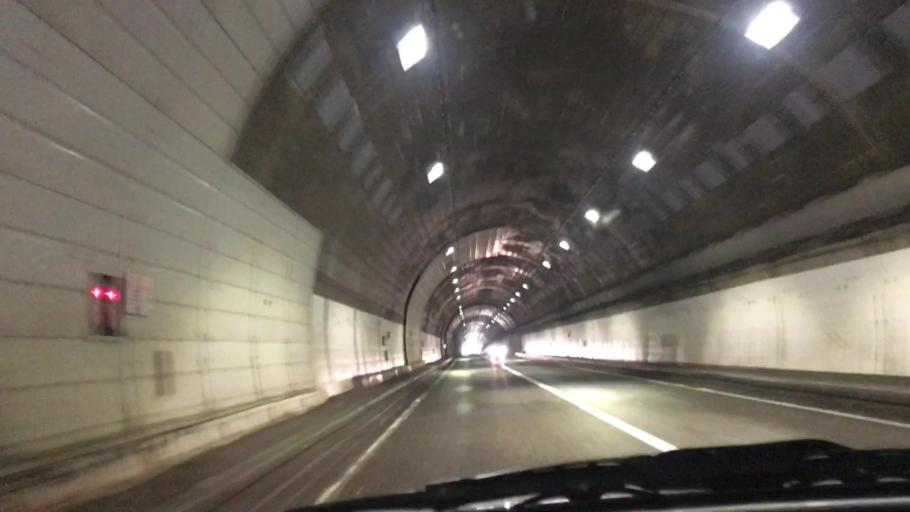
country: JP
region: Hokkaido
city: Otofuke
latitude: 43.3690
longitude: 143.2092
